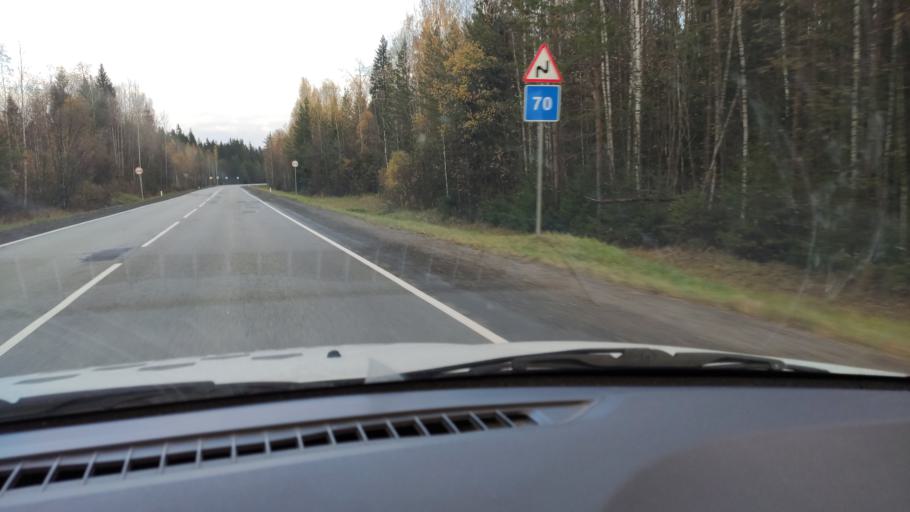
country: RU
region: Kirov
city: Belaya Kholunitsa
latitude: 58.9033
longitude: 50.9388
